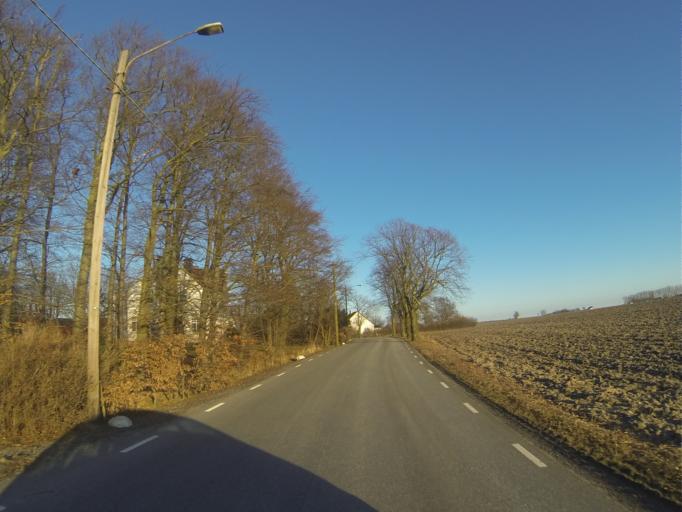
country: SE
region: Skane
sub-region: Malmo
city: Tygelsjo
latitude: 55.5426
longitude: 13.0199
